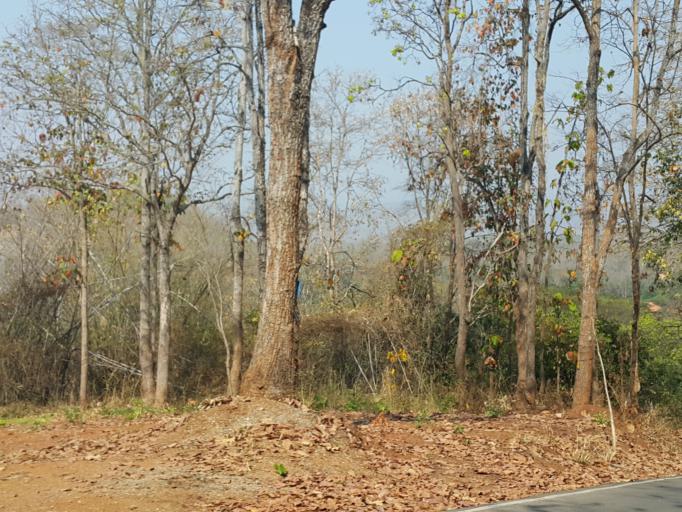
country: TH
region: Chiang Mai
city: Mae On
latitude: 18.7866
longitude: 99.2363
